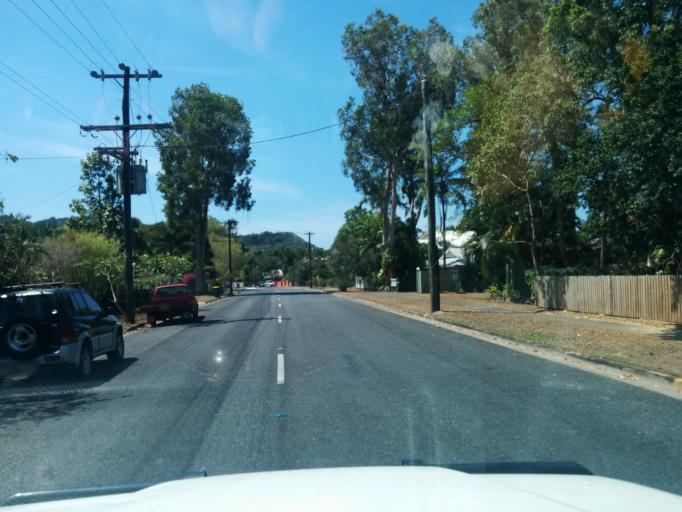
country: AU
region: Queensland
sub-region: Cairns
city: Cairns
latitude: -16.9078
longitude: 145.7552
